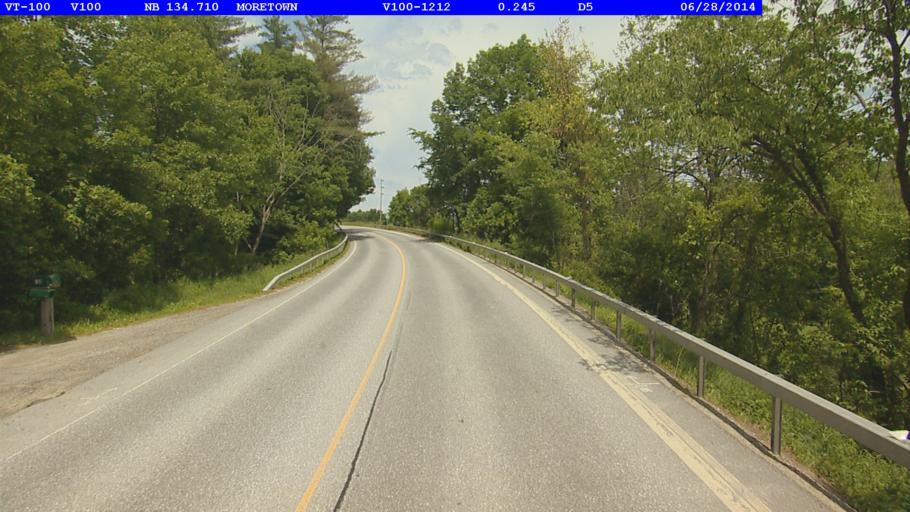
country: US
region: Vermont
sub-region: Washington County
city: Waterbury
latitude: 44.2375
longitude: -72.7767
